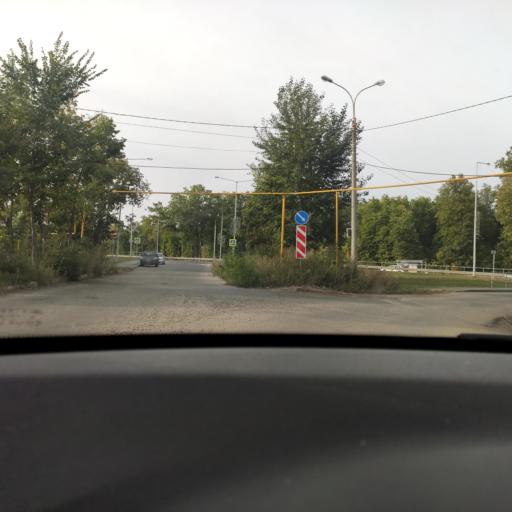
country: RU
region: Samara
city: Volzhskiy
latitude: 53.3566
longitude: 50.2099
